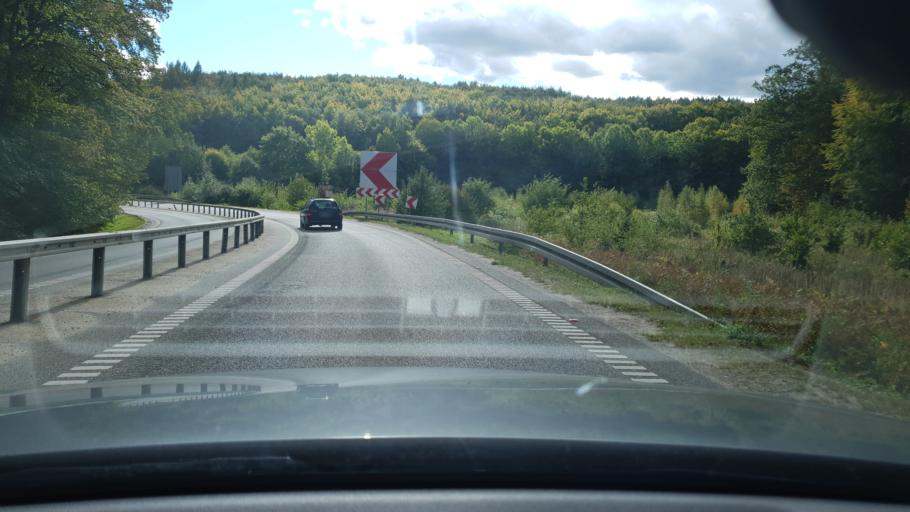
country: PL
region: Pomeranian Voivodeship
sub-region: Powiat wejherowski
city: Reda
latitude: 54.6227
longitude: 18.3388
